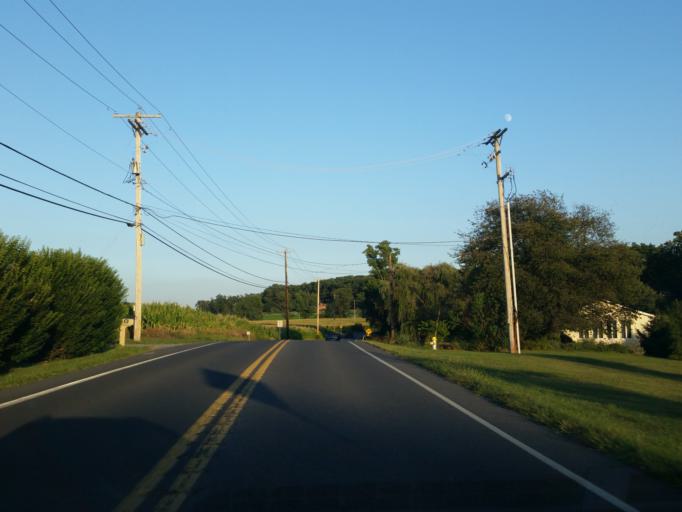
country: US
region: Pennsylvania
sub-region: Lebanon County
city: Sand Hill
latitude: 40.3740
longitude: -76.4359
